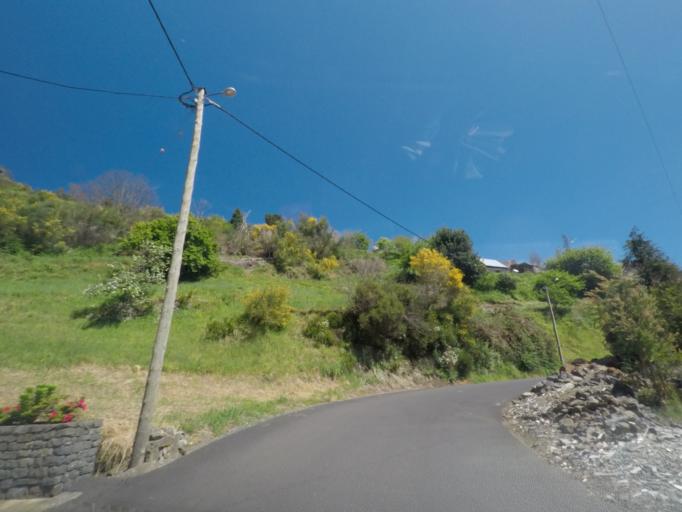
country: PT
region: Madeira
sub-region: Calheta
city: Arco da Calheta
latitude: 32.7285
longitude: -17.1289
